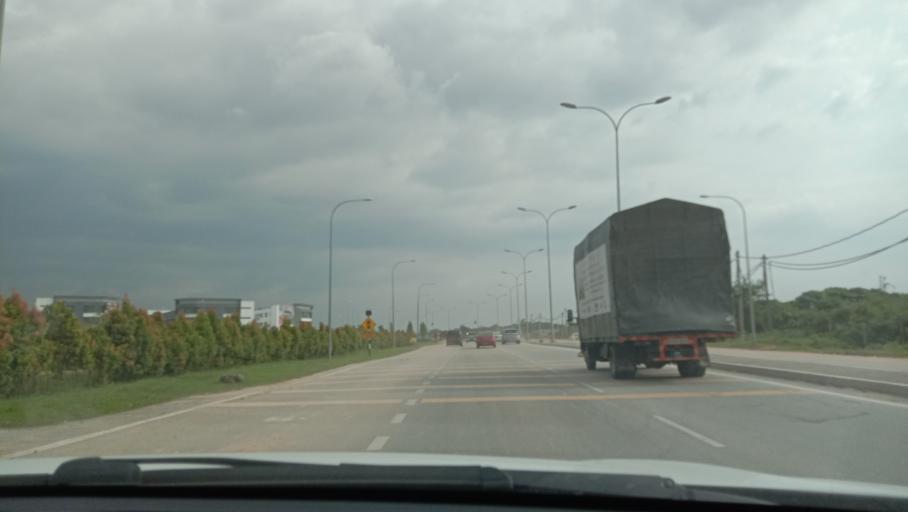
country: MY
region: Selangor
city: Ladang Seri Kundang
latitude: 3.2448
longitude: 101.4733
